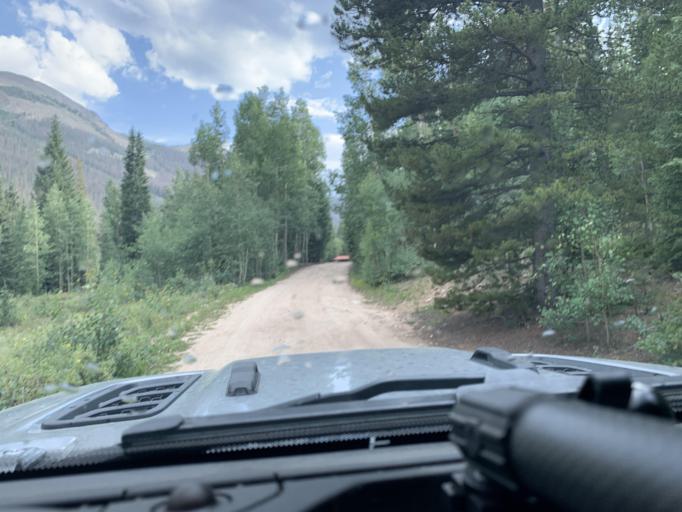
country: US
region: Colorado
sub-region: Chaffee County
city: Buena Vista
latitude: 38.6957
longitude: -106.3512
